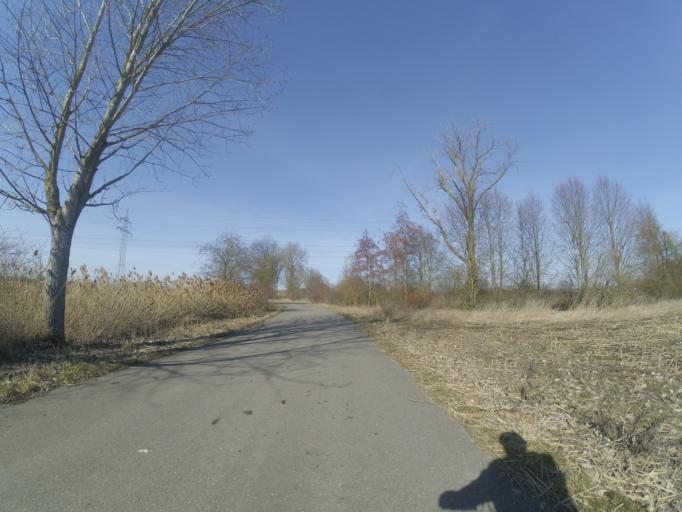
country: DE
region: Baden-Wuerttemberg
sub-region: Tuebingen Region
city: Rammingen
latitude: 48.4992
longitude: 10.1929
